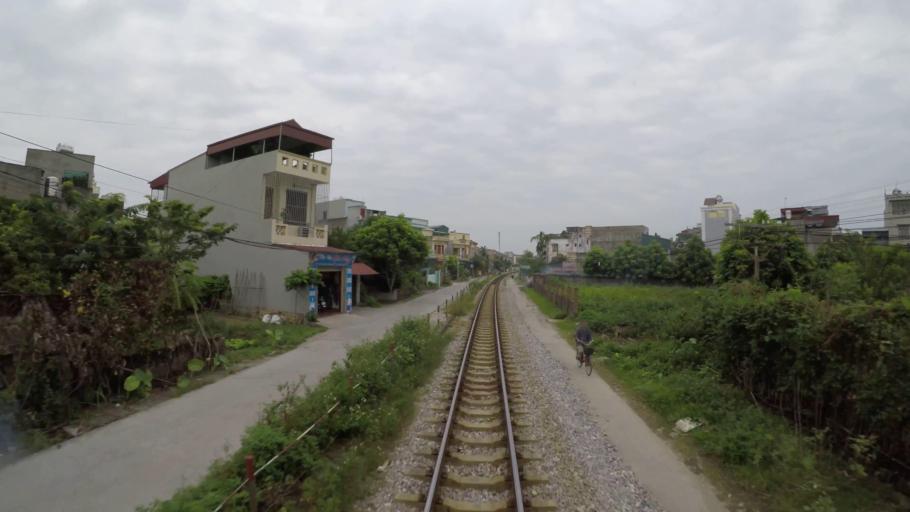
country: VN
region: Hai Duong
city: Lai Cach
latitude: 20.9434
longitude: 106.2863
